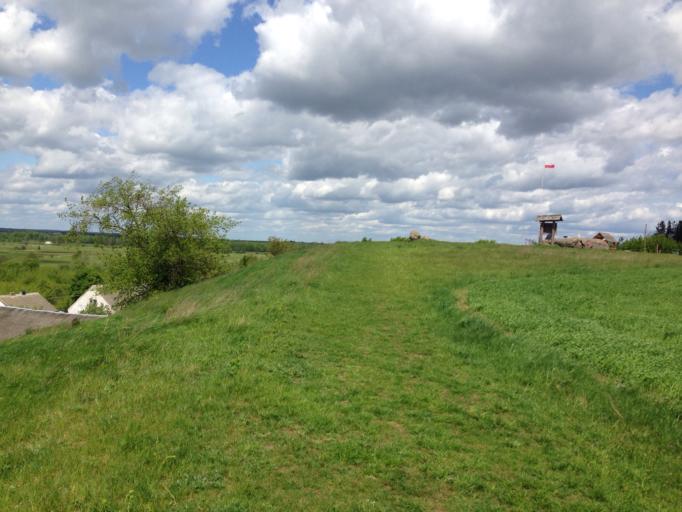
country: PL
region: Podlasie
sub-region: Powiat lomzynski
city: Wizna
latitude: 53.2117
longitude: 22.4891
